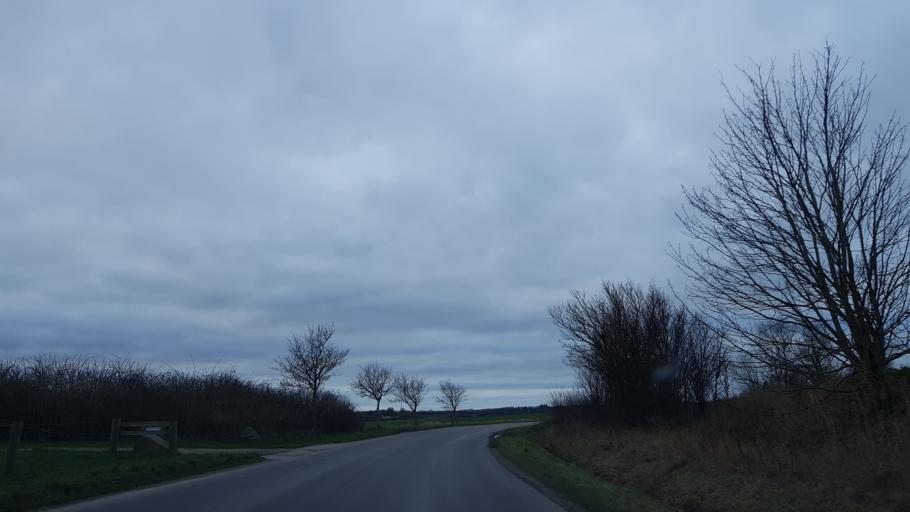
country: DK
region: Zealand
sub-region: Odsherred Kommune
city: Hojby
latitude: 55.9265
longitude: 11.5517
